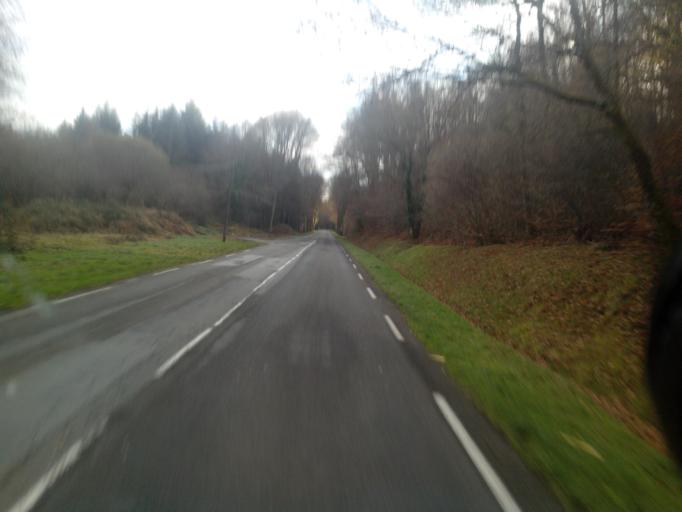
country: FR
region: Limousin
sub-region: Departement de la Haute-Vienne
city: Eymoutiers
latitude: 45.6585
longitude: 1.8220
